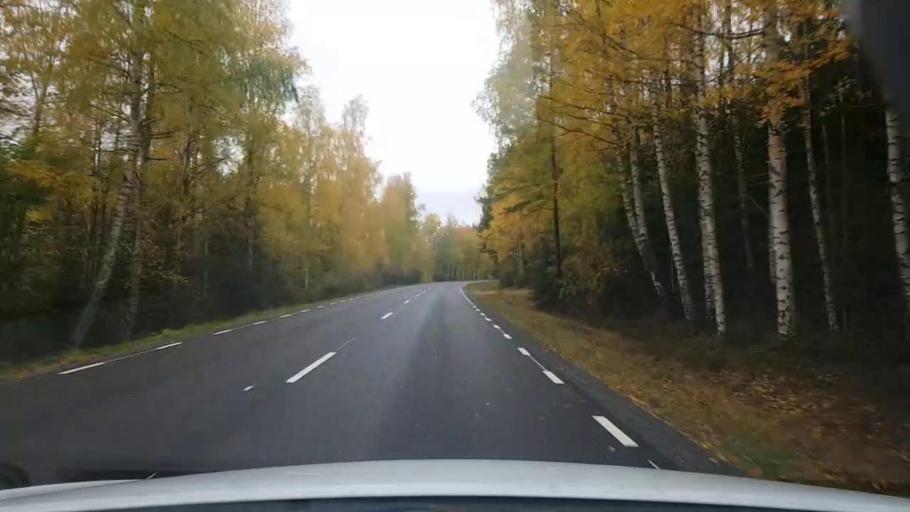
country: SE
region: OErebro
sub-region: Laxa Kommun
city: Laxa
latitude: 58.8210
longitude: 14.5488
